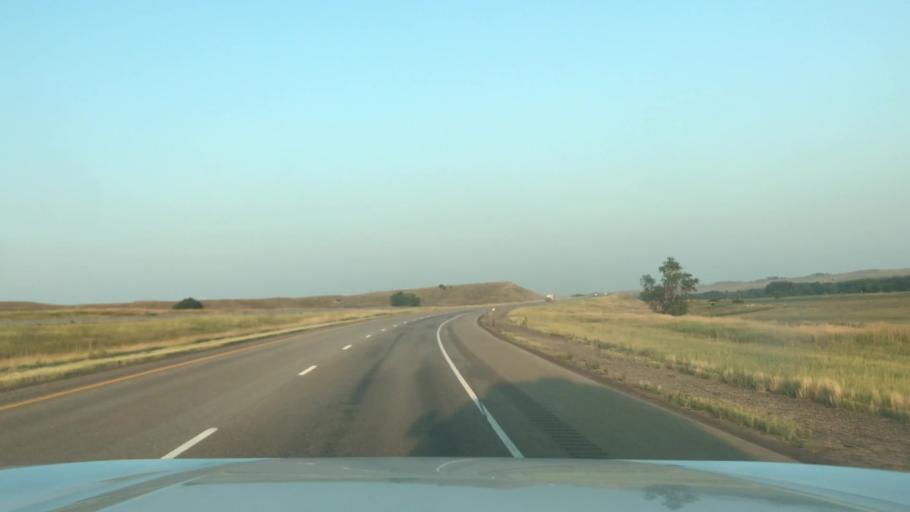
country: US
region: Wyoming
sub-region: Sheridan County
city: Sheridan
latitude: 44.9181
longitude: -107.1027
